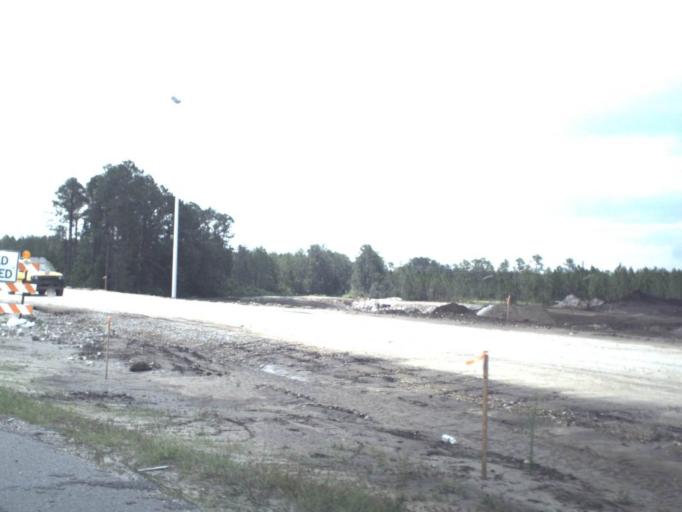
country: US
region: Florida
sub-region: Clay County
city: Bellair-Meadowbrook Terrace
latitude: 30.2509
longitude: -81.8481
